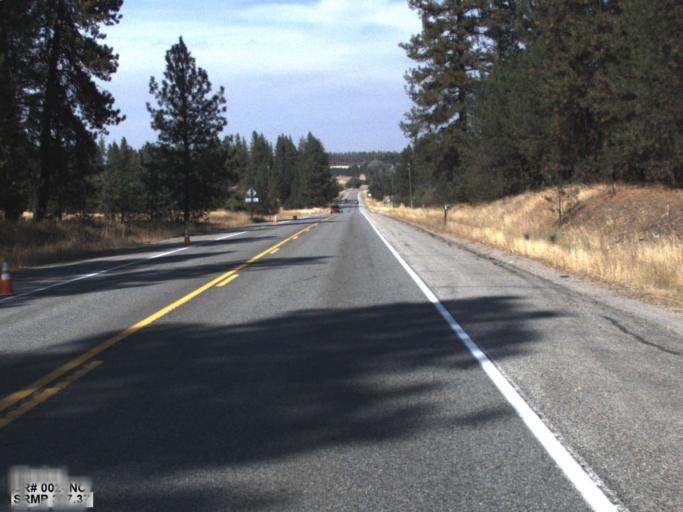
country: US
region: Washington
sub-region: Spokane County
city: Deer Park
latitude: 47.9309
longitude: -117.3514
